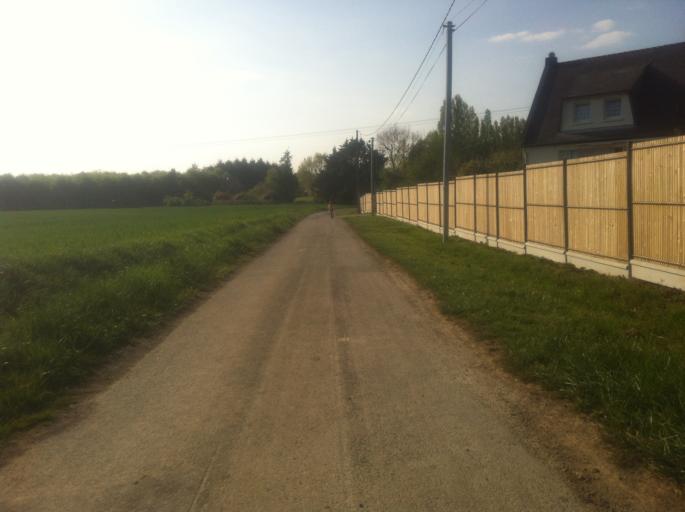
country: FR
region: Brittany
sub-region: Departement d'Ille-et-Vilaine
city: Bruz
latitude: 48.0127
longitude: -1.7253
